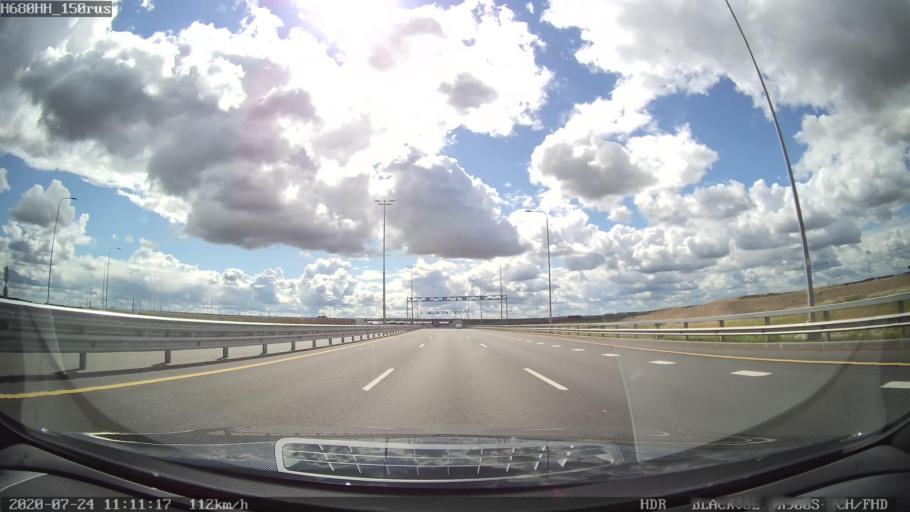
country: RU
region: St.-Petersburg
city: Tyarlevo
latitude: 59.7251
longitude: 30.5133
